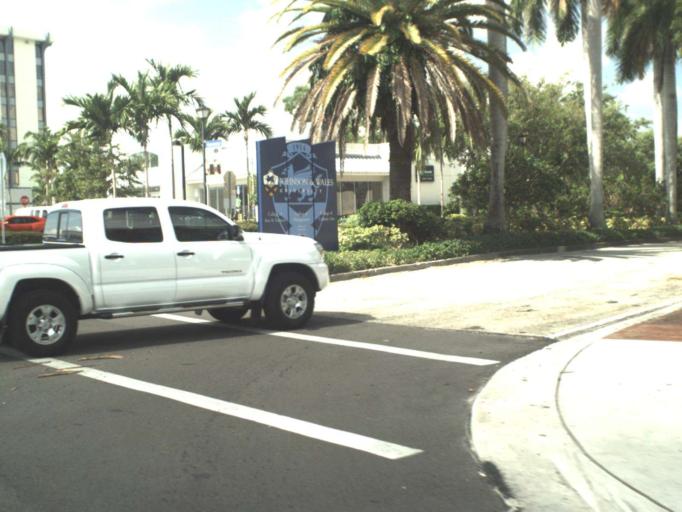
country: US
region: Florida
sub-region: Miami-Dade County
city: Biscayne Park
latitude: 25.8936
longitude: -80.1626
